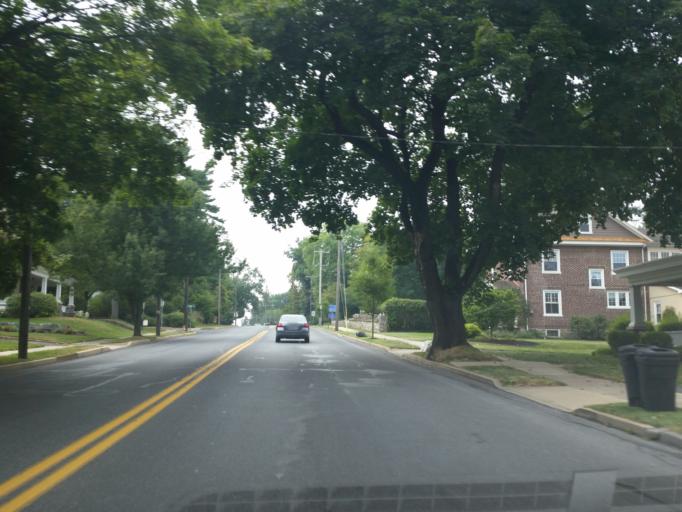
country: US
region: Pennsylvania
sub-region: Lancaster County
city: Lititz
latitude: 40.1489
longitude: -76.3066
